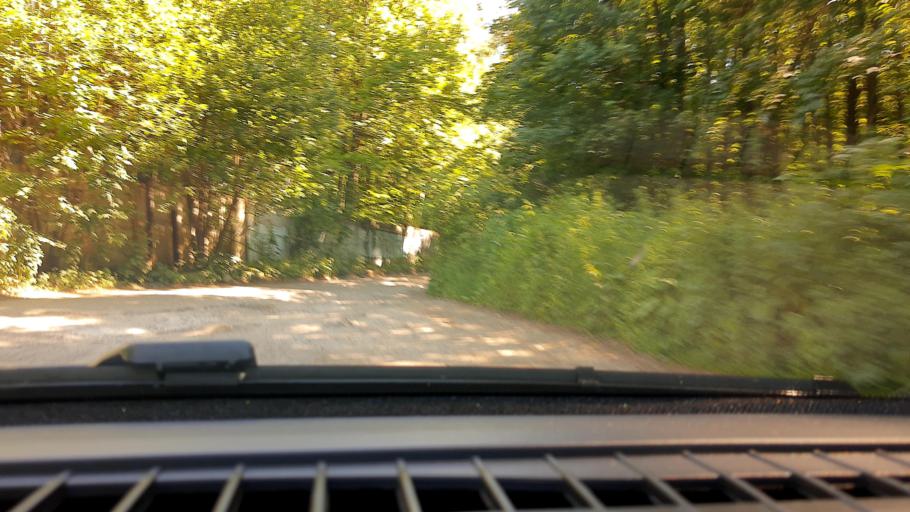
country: RU
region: Nizjnij Novgorod
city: Nizhniy Novgorod
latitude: 56.2282
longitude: 43.9332
